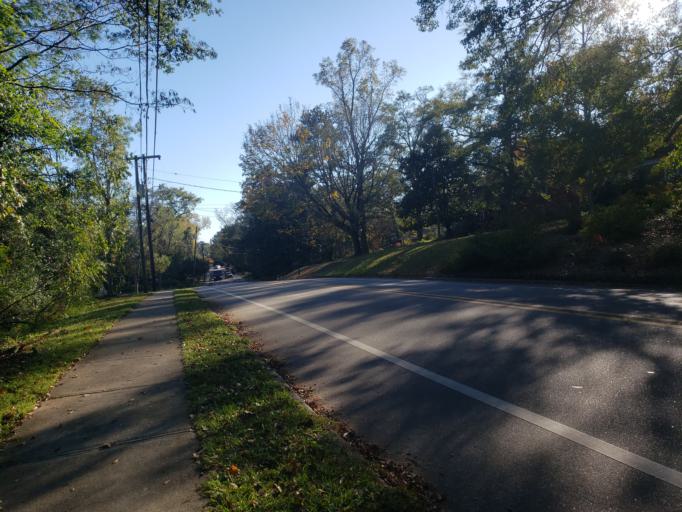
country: US
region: Alabama
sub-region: Lee County
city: Auburn
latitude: 32.5961
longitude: -85.4798
